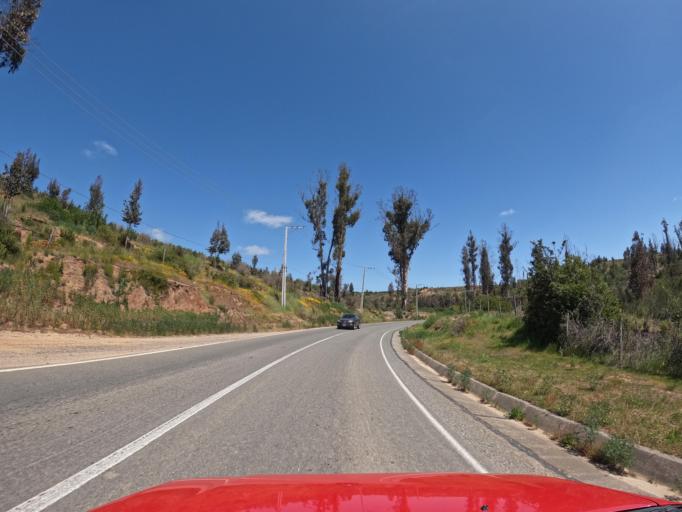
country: CL
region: O'Higgins
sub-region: Provincia de Colchagua
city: Santa Cruz
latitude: -34.6618
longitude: -71.8514
